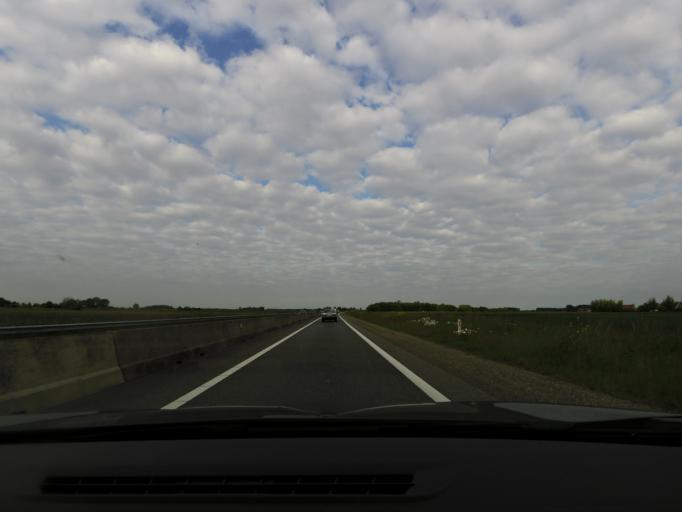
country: NL
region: South Holland
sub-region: Gemeente Hellevoetsluis
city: Nieuwenhoorn
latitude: 51.8588
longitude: 4.1442
